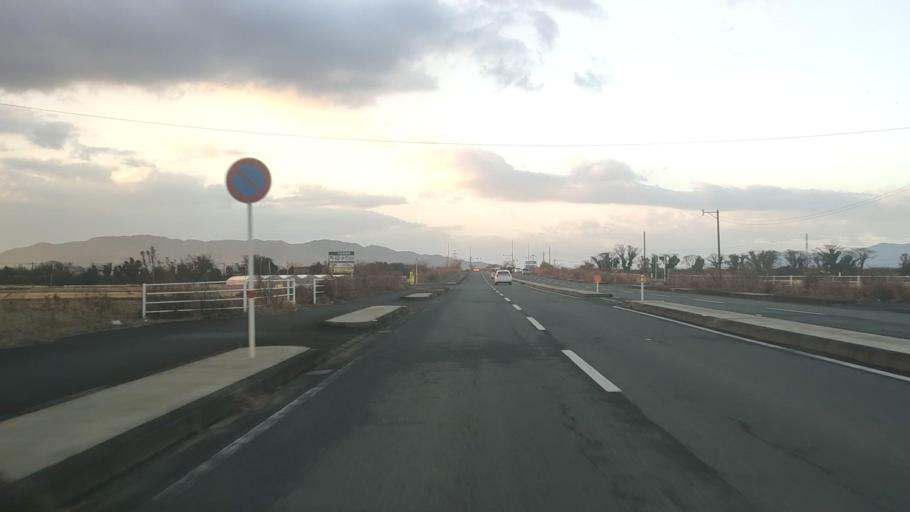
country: JP
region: Kumamoto
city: Kumamoto
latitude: 32.7455
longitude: 130.7062
